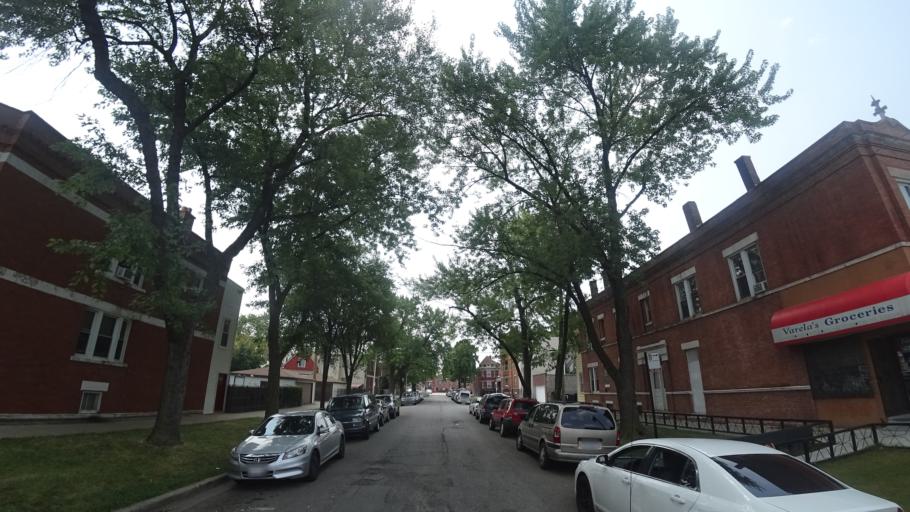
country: US
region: Illinois
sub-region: Cook County
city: Cicero
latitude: 41.8460
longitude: -87.7262
